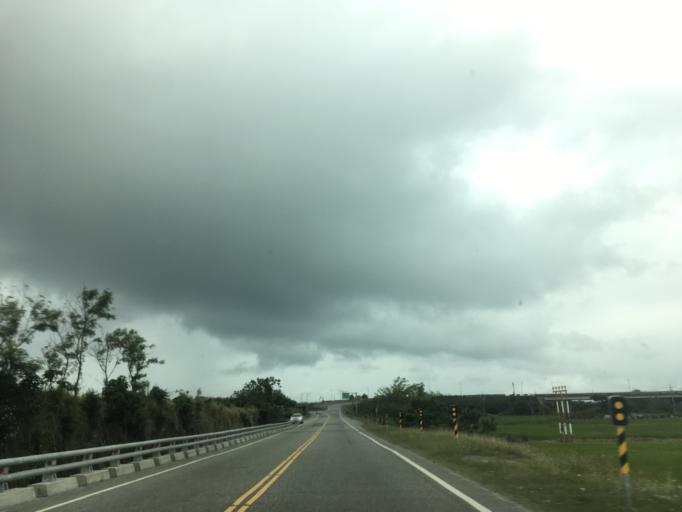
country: TW
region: Taiwan
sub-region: Taitung
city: Taitung
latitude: 22.7777
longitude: 121.1700
